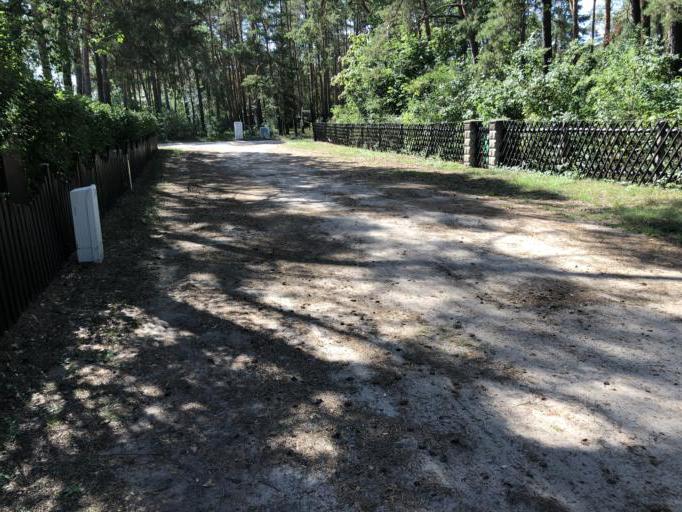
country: DE
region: Brandenburg
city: Am Mellensee
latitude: 52.1736
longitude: 13.3964
